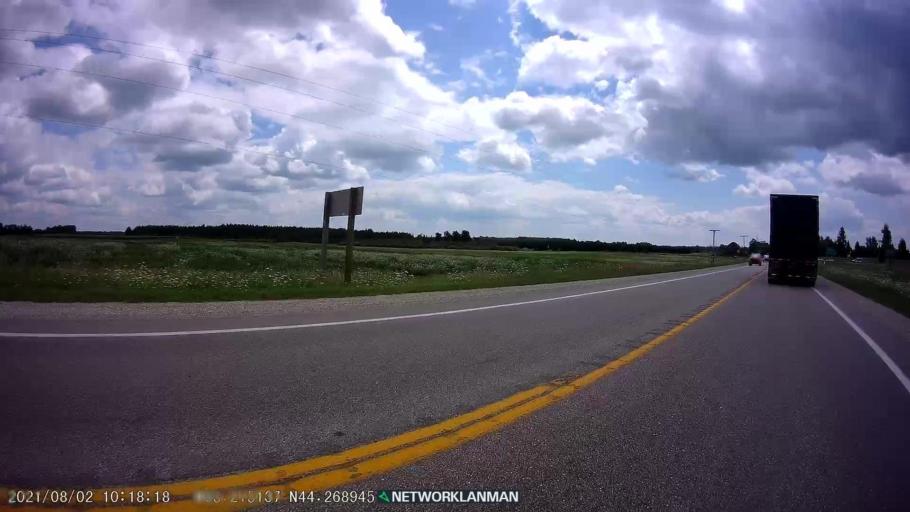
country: US
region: Michigan
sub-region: Missaukee County
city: Lake City
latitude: 44.2679
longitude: -85.2144
